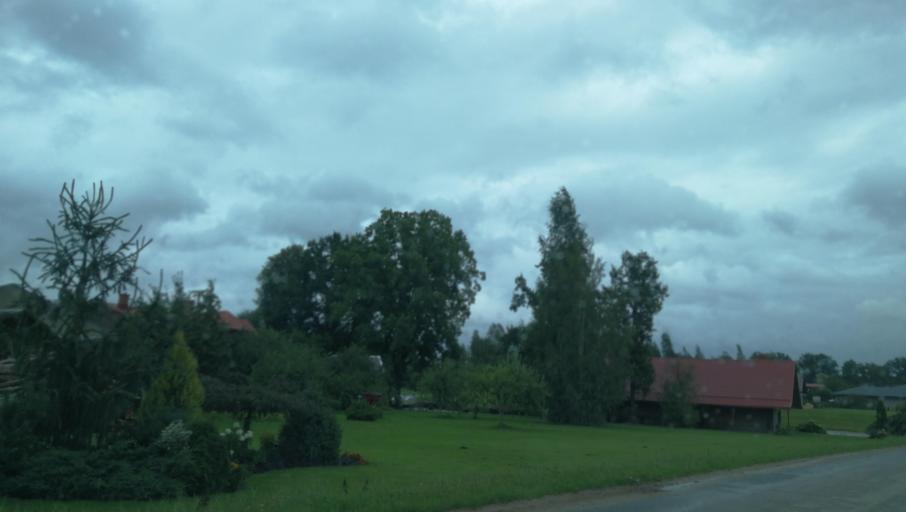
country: LV
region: Beverina
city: Murmuiza
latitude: 57.4703
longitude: 25.4870
